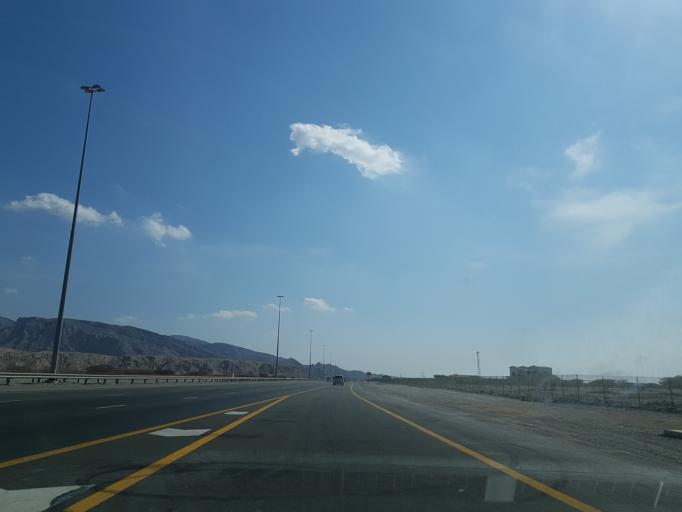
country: AE
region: Ra's al Khaymah
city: Ras al-Khaimah
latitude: 25.7950
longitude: 56.0307
